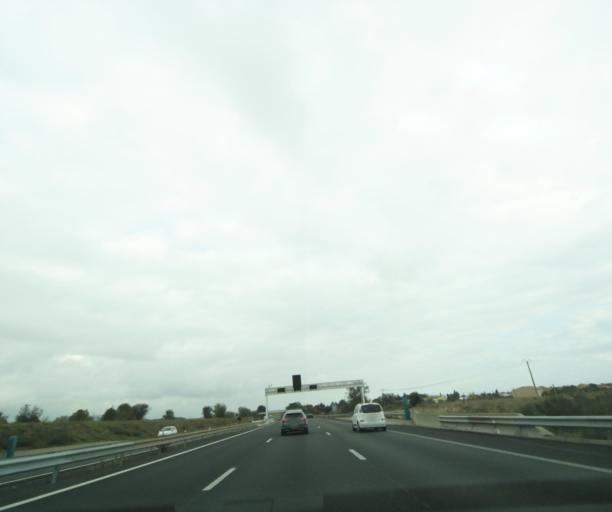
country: FR
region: Languedoc-Roussillon
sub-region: Departement de l'Herault
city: Pinet
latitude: 43.4085
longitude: 3.4996
